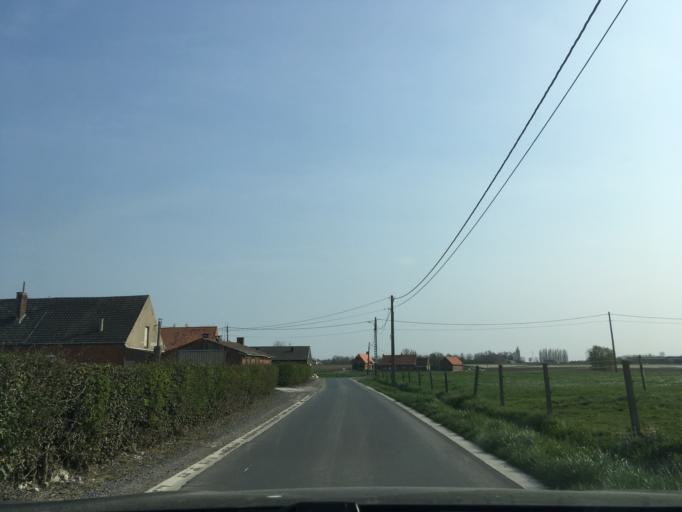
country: BE
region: Flanders
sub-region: Provincie West-Vlaanderen
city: Ardooie
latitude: 50.9859
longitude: 3.2095
